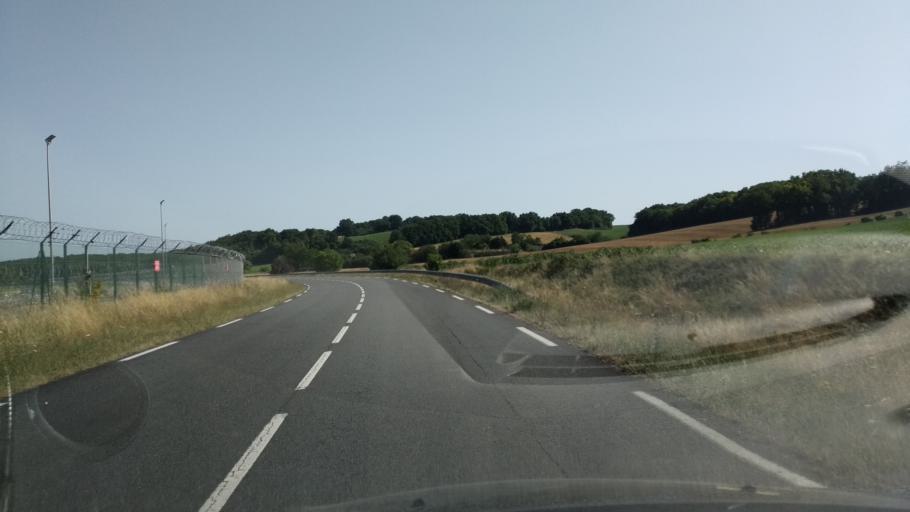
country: FR
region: Poitou-Charentes
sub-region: Departement de la Vienne
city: Lussac-les-Chateaux
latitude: 46.4534
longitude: 0.6476
